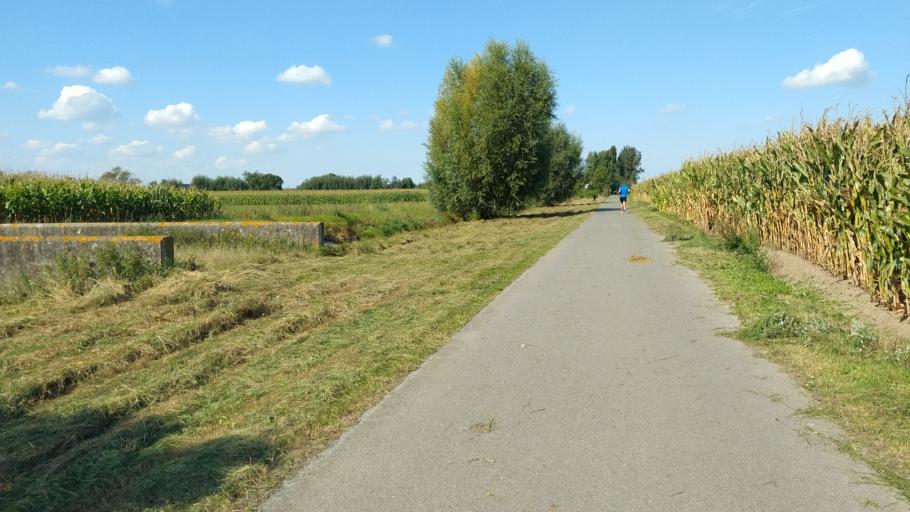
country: BE
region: Flanders
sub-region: Provincie Oost-Vlaanderen
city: Assenede
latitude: 51.2312
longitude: 3.7383
